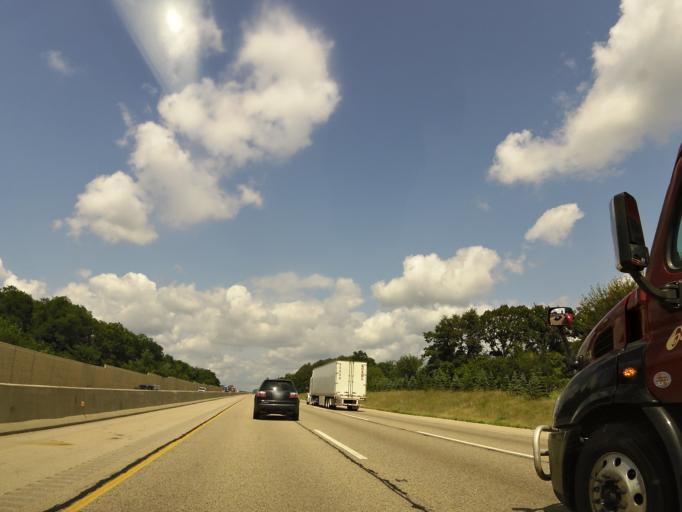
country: US
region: Illinois
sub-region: Winnebago County
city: Roscoe
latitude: 42.3981
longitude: -88.9794
